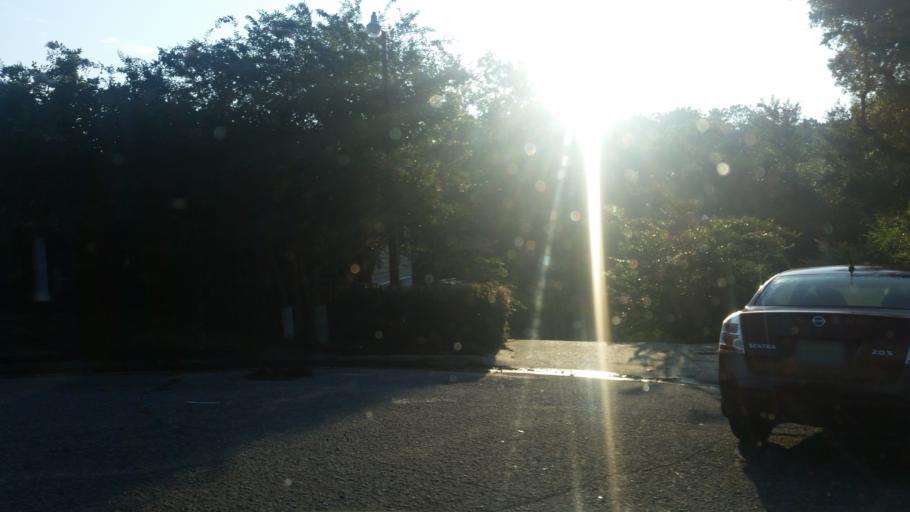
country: US
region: Florida
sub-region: Escambia County
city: Ferry Pass
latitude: 30.5417
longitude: -87.2255
